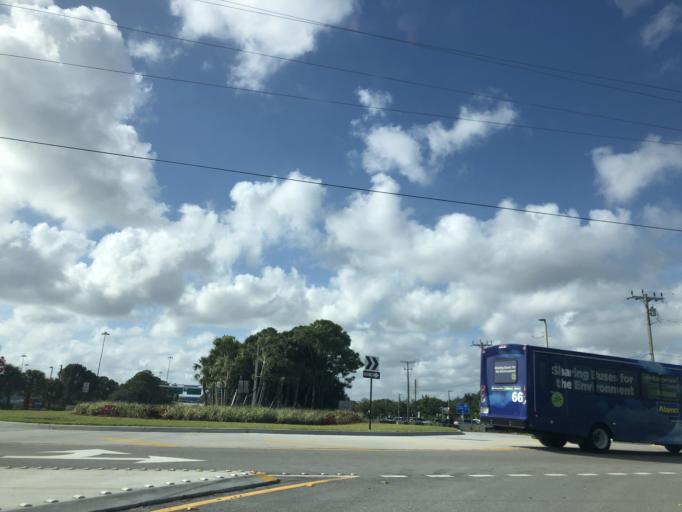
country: US
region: Florida
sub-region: Palm Beach County
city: West Palm Beach
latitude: 26.6895
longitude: -80.0787
